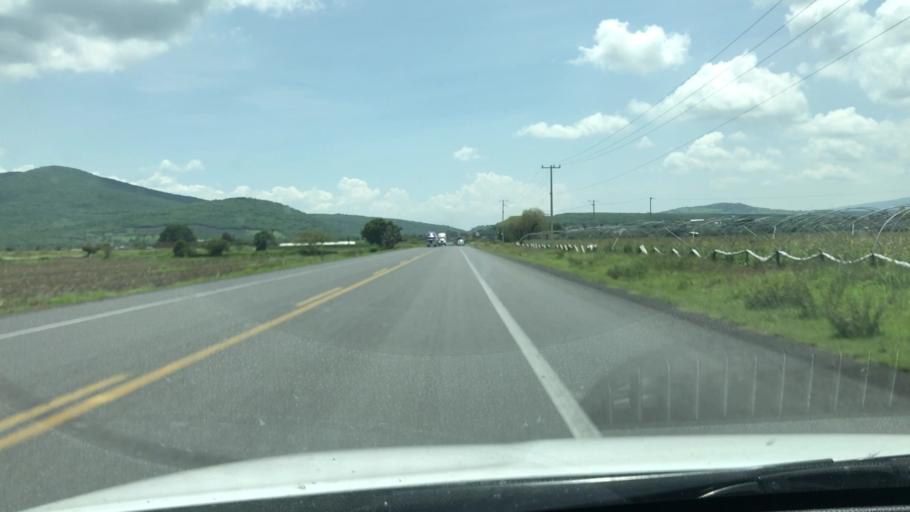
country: MX
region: Michoacan
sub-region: Yurecuaro
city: Yurecuaro
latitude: 20.3266
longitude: -102.2728
